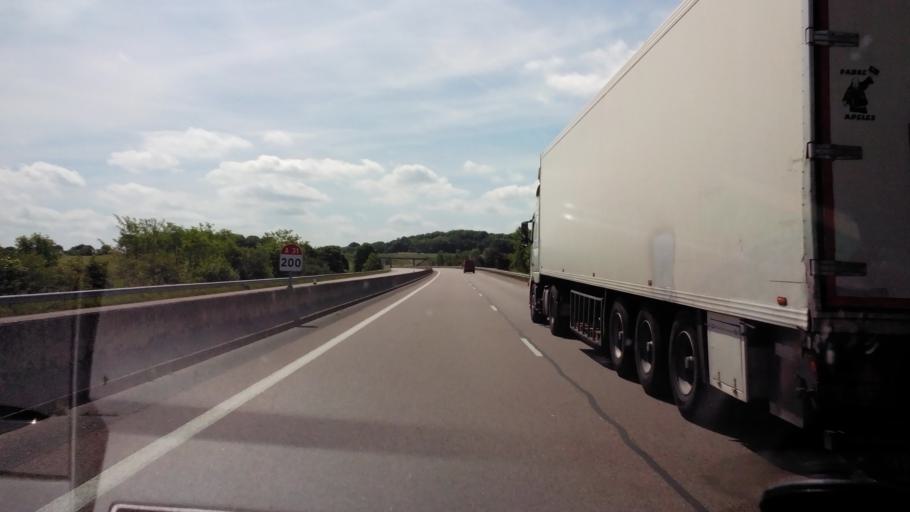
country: FR
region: Lorraine
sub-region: Departement de Meurthe-et-Moselle
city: Colombey-les-Belles
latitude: 48.4154
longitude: 5.8642
